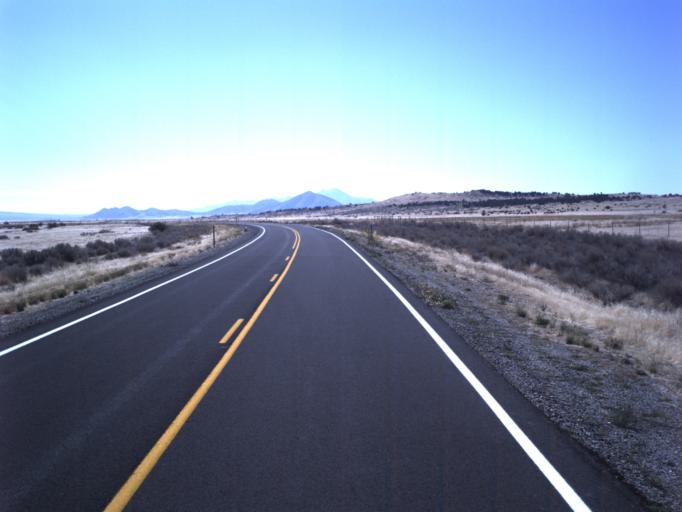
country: US
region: Utah
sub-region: Tooele County
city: Grantsville
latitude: 40.2583
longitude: -112.7404
